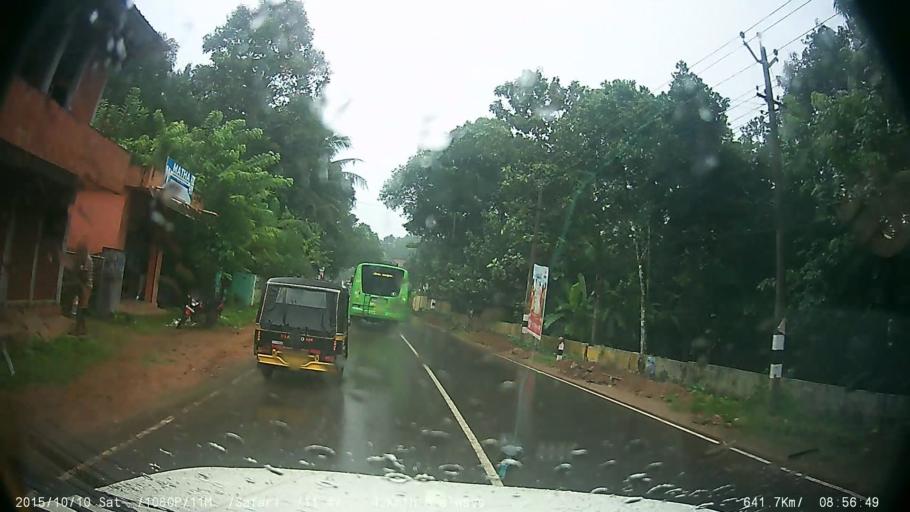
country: IN
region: Kerala
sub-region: Kottayam
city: Palackattumala
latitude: 9.6923
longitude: 76.5522
